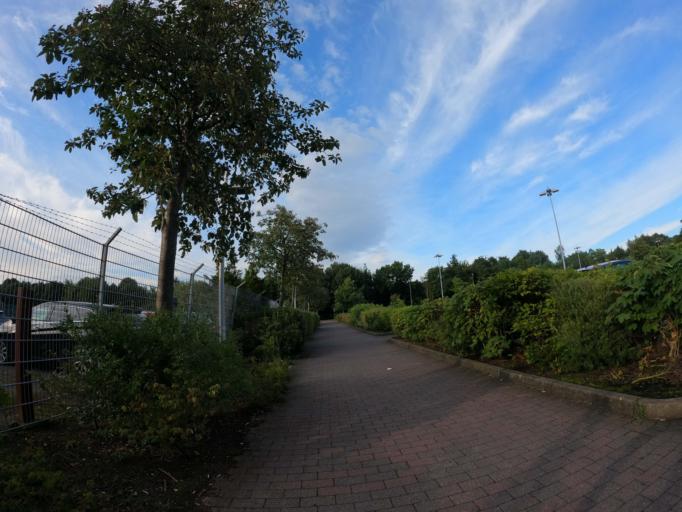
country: DE
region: Mecklenburg-Vorpommern
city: Kramerhof
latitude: 54.3214
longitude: 13.0481
